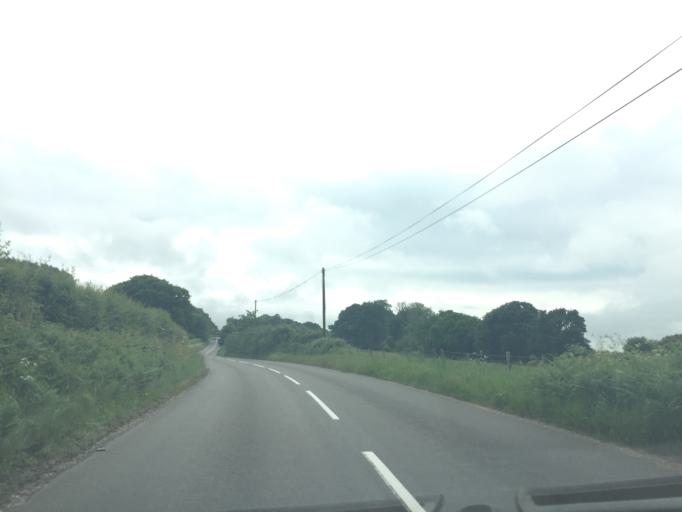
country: GB
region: England
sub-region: Dorset
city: Wareham
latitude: 50.6766
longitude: -2.1578
